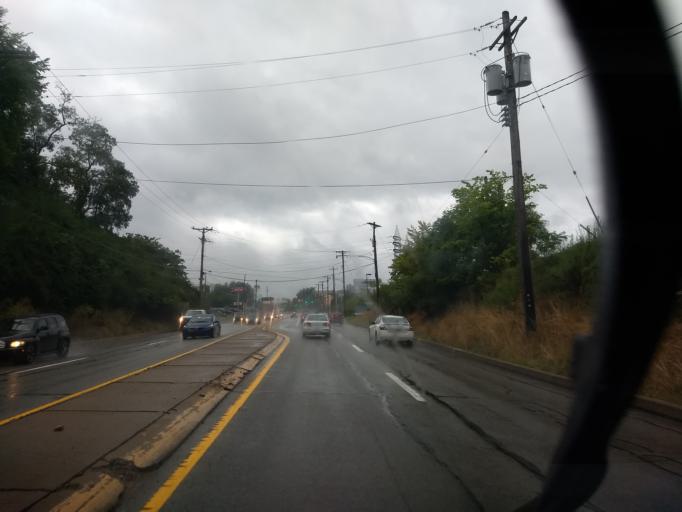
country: US
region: Pennsylvania
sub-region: Allegheny County
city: East Pittsburgh
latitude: 40.3858
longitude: -79.8260
